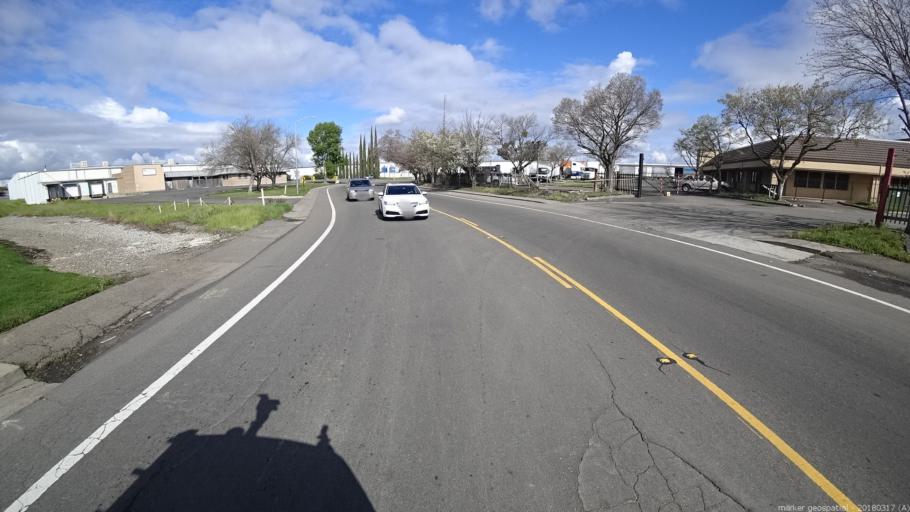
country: US
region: California
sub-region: Sacramento County
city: Florin
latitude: 38.4776
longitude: -121.3969
